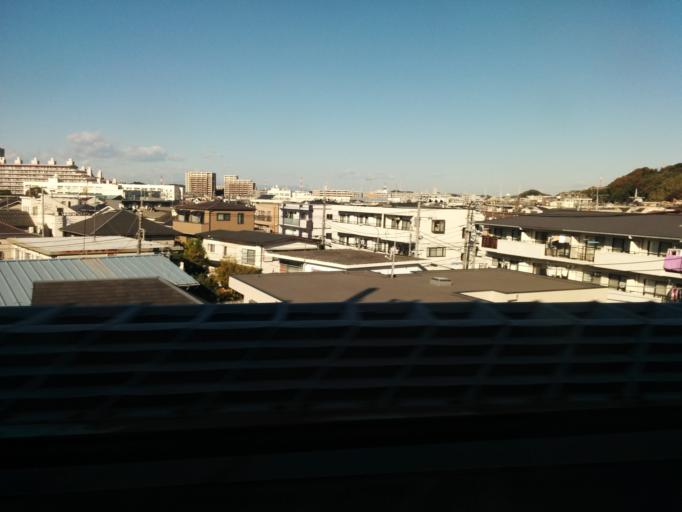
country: JP
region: Kanagawa
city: Yokohama
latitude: 35.5176
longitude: 139.6294
